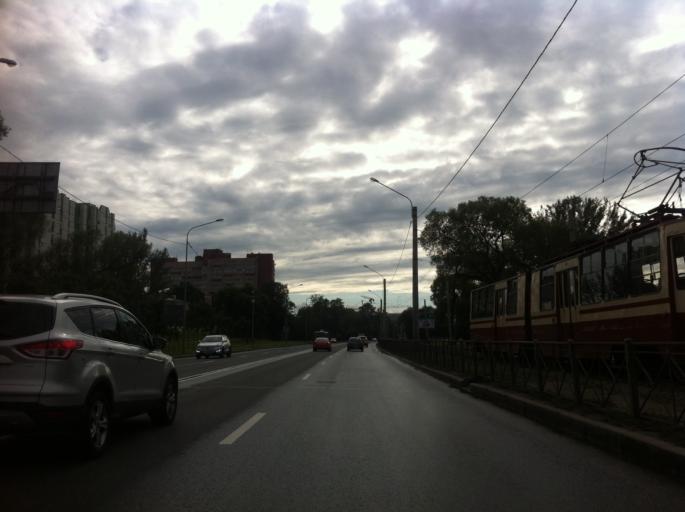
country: RU
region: St.-Petersburg
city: Dachnoye
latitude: 59.8507
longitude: 30.2340
